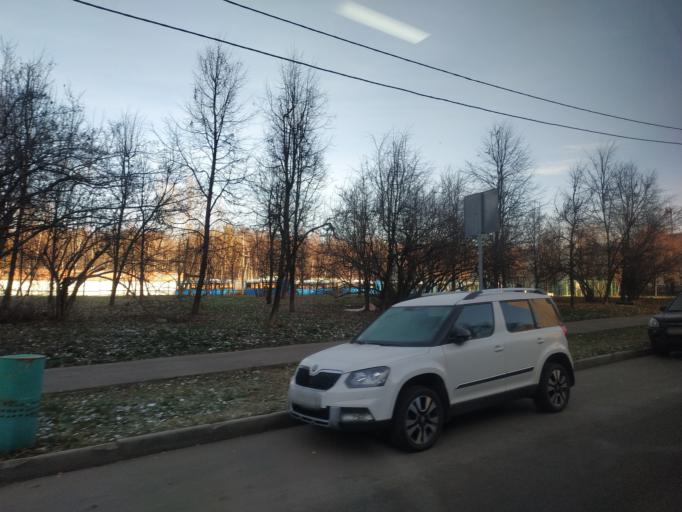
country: RU
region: Moscow
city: Biryulevo
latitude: 55.5856
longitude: 37.6905
